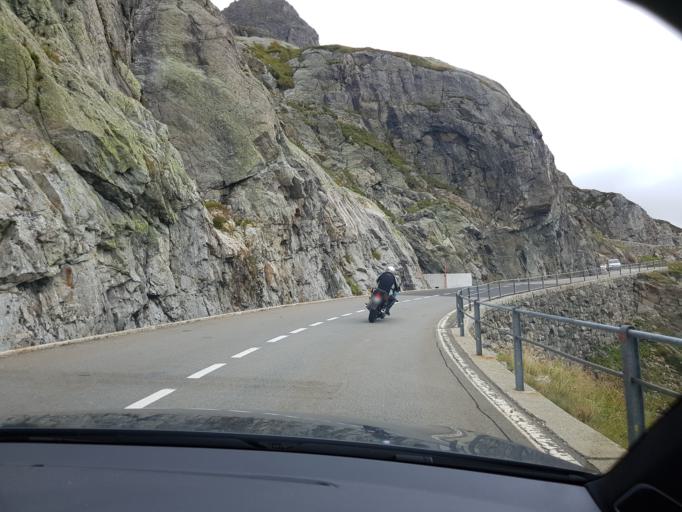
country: CH
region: Obwalden
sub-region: Obwalden
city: Engelberg
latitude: 46.7386
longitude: 8.4544
